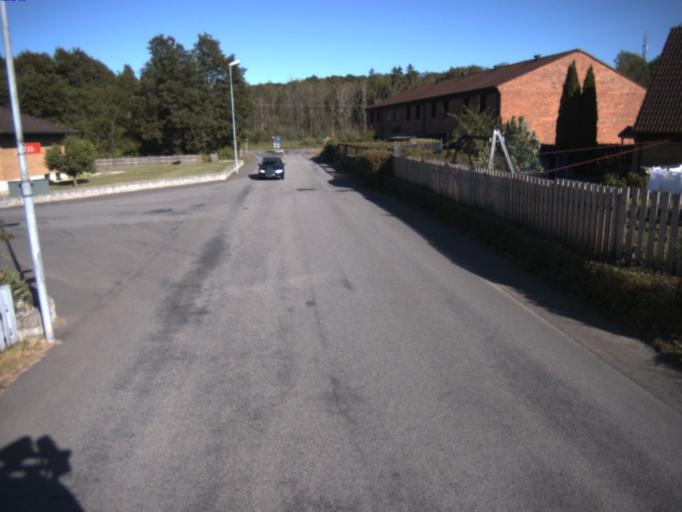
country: SE
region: Skane
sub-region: Helsingborg
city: Odakra
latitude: 56.0977
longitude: 12.7618
